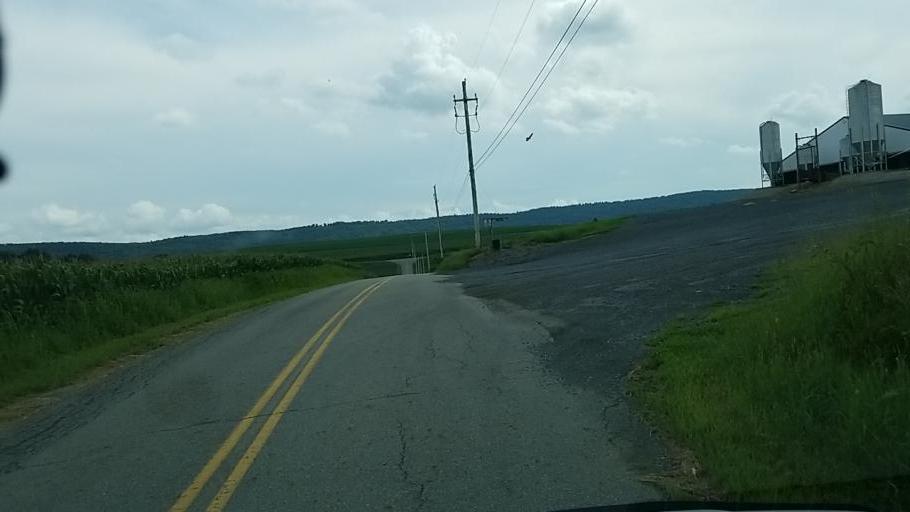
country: US
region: Pennsylvania
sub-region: Dauphin County
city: Elizabethville
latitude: 40.6524
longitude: -76.8351
